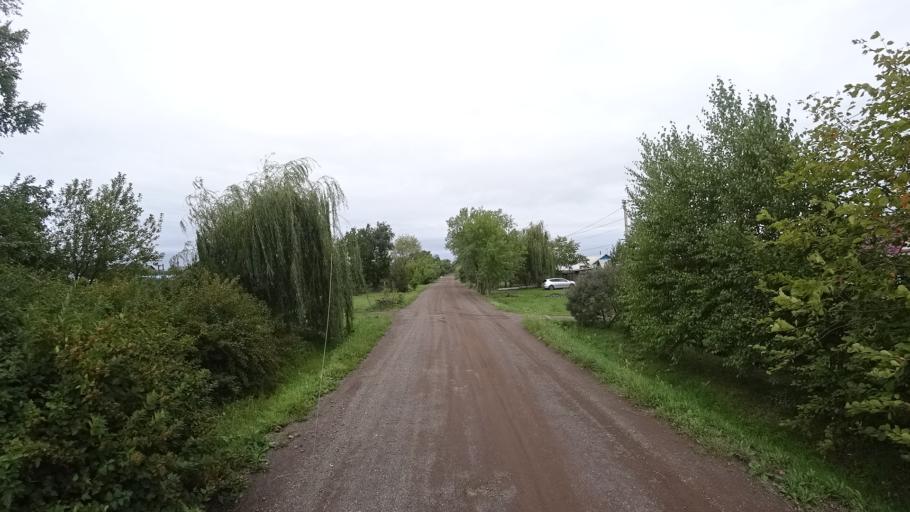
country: RU
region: Primorskiy
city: Chernigovka
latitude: 44.3340
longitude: 132.5684
